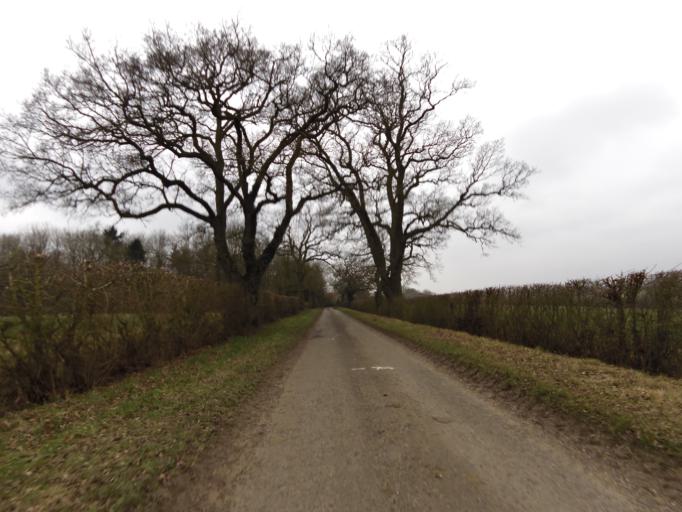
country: GB
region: England
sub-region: Suffolk
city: Cookley
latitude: 52.2529
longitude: 1.4128
